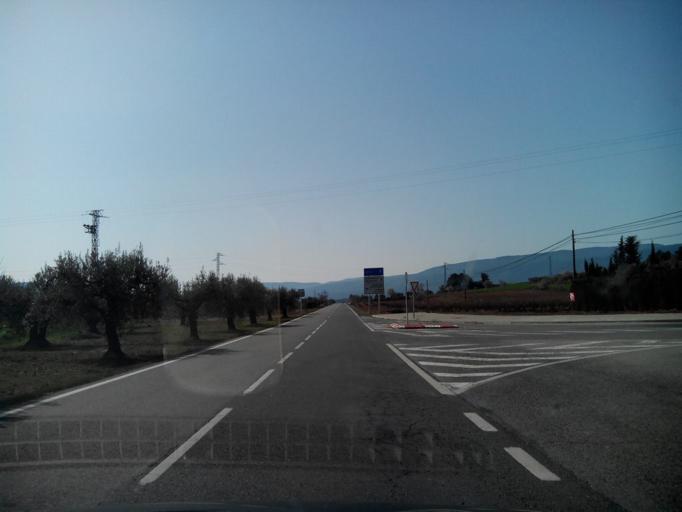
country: ES
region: Catalonia
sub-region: Provincia de Tarragona
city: Blancafort
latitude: 41.4090
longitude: 1.1958
